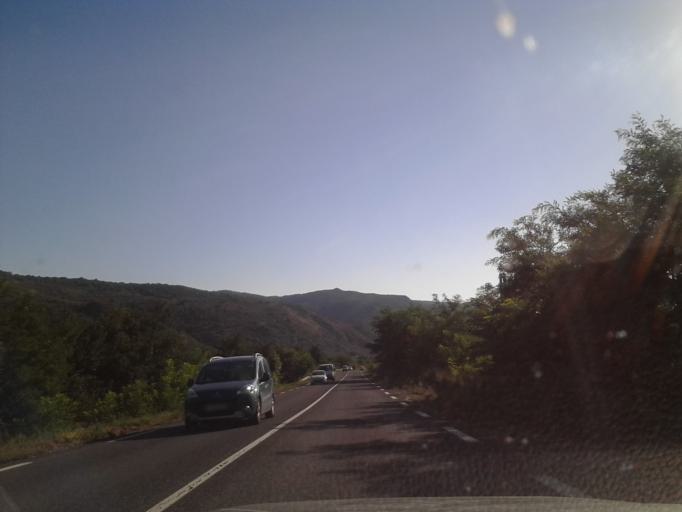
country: FR
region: Languedoc-Roussillon
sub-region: Departement des Pyrenees-Orientales
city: Prades
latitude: 42.6350
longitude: 2.4669
